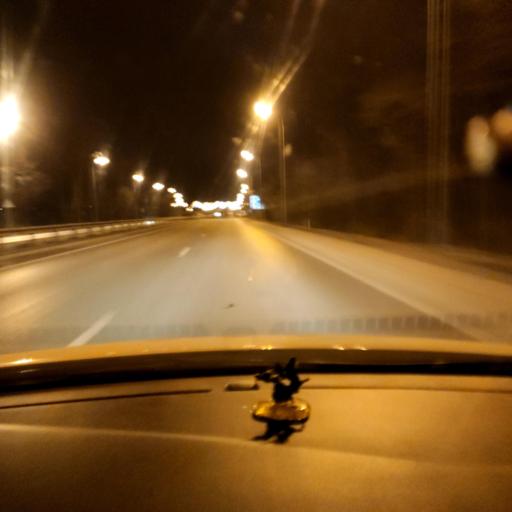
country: RU
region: Tatarstan
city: Osinovo
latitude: 55.8504
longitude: 48.8535
